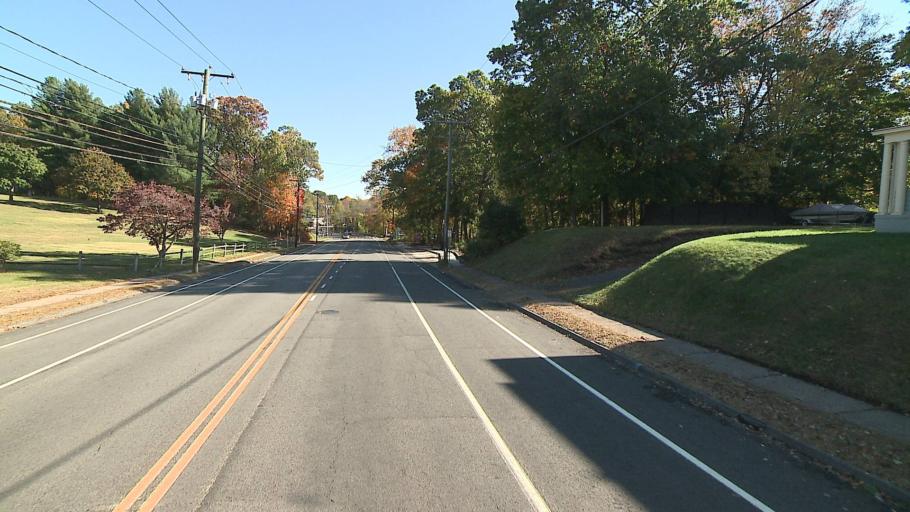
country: US
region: Connecticut
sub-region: Hartford County
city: East Hartford
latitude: 41.7817
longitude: -72.5983
